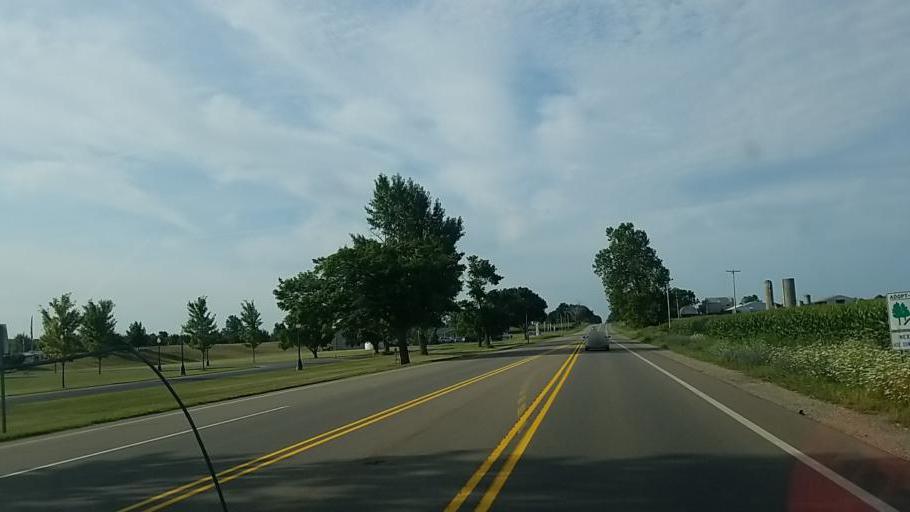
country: US
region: Michigan
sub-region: Ionia County
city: Ionia
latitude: 42.9145
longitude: -85.0748
